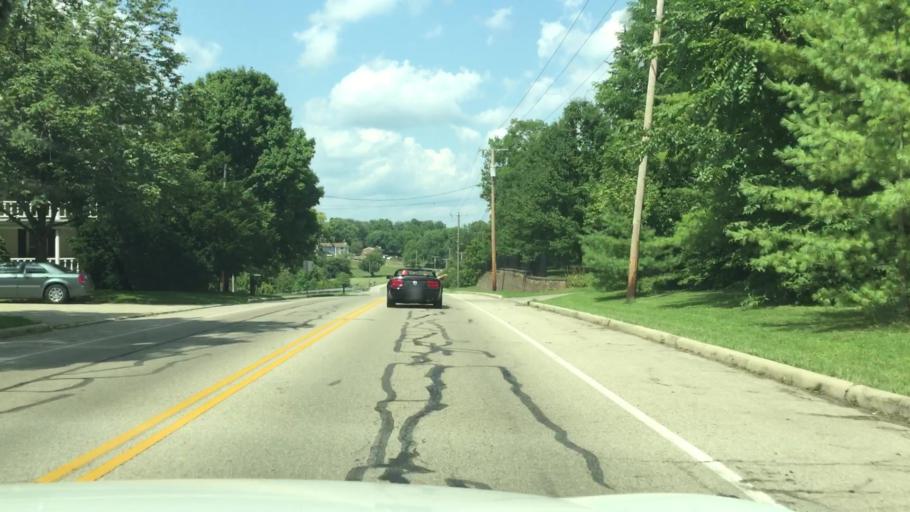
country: US
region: Ohio
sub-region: Clark County
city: Northridge
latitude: 39.9327
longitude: -83.7335
